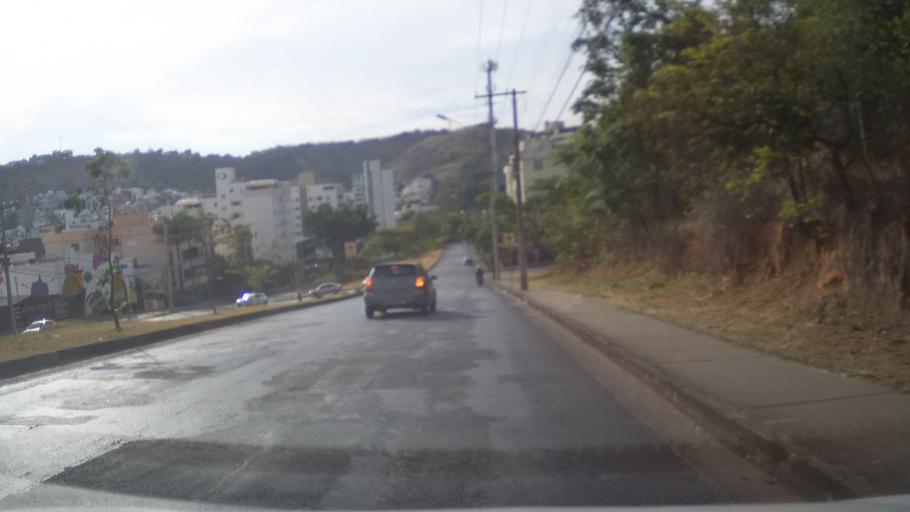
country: BR
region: Minas Gerais
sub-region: Belo Horizonte
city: Belo Horizonte
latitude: -19.8837
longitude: -43.9977
